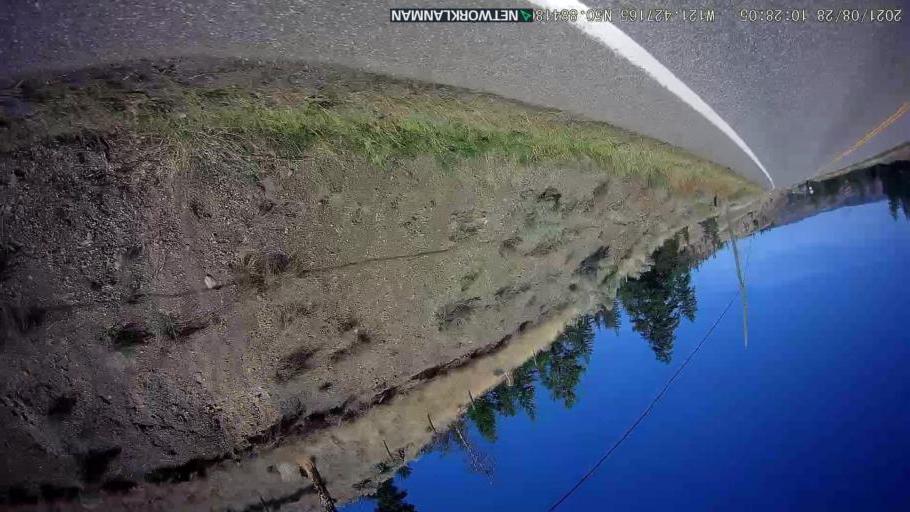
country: CA
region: British Columbia
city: Cache Creek
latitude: 50.8842
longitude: -121.4274
